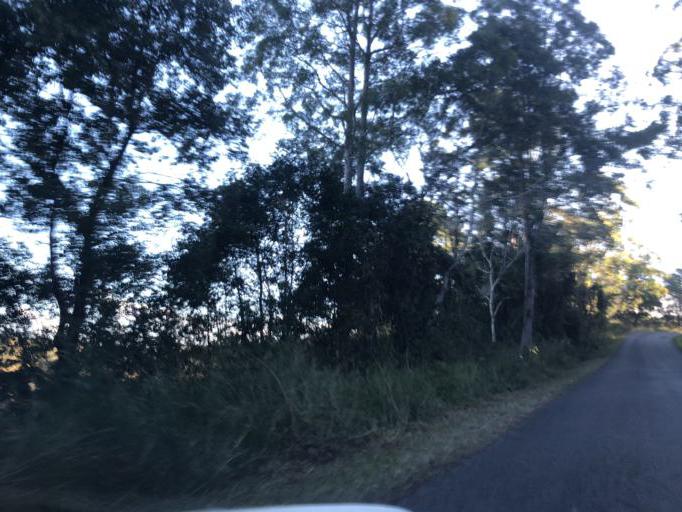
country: AU
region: New South Wales
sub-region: Nambucca Shire
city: Nambucca
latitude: -30.5827
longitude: 152.9427
